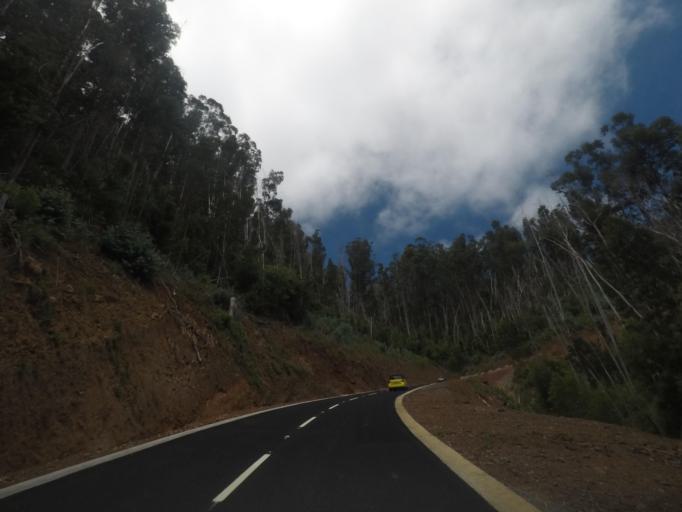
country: PT
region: Madeira
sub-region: Calheta
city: Estreito da Calheta
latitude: 32.7473
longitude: -17.1576
